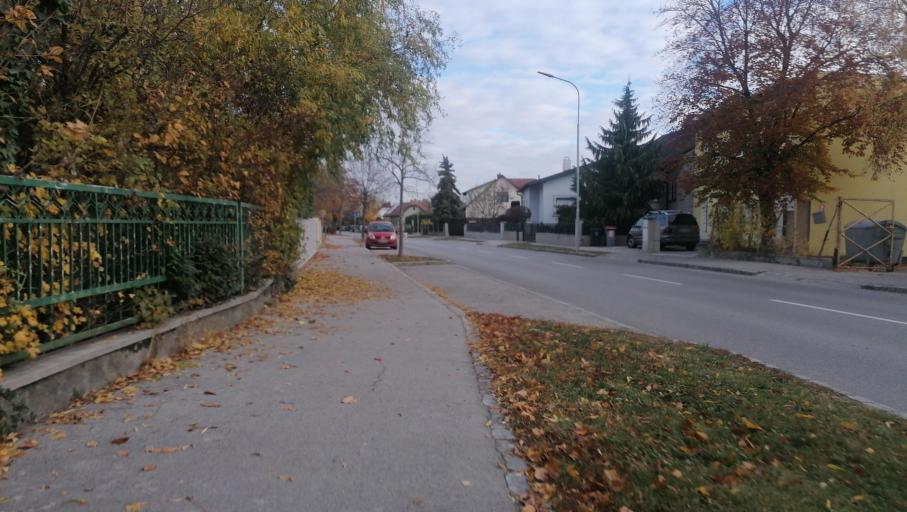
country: AT
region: Lower Austria
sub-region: Politischer Bezirk Baden
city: Oberwaltersdorf
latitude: 47.9690
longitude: 16.3191
